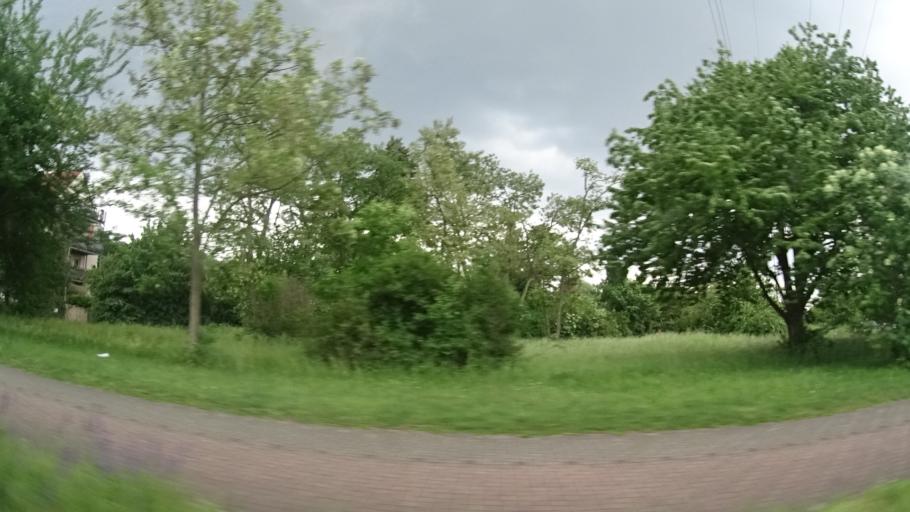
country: DE
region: Rheinland-Pfalz
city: Gartenstadt
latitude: 49.4667
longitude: 8.4132
